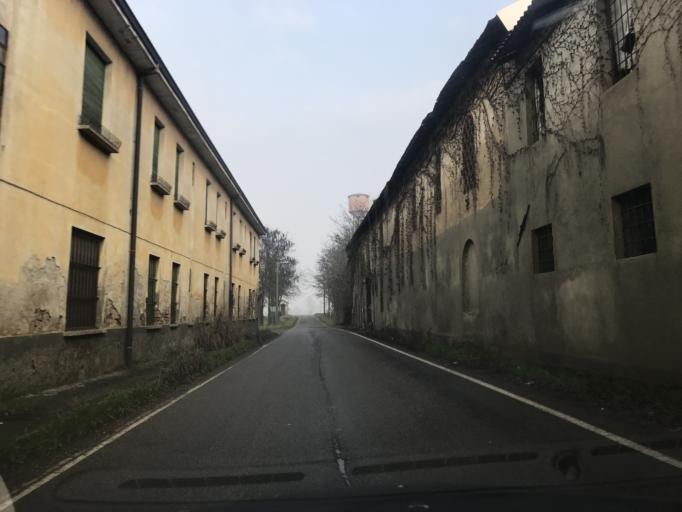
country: IT
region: Lombardy
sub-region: Provincia di Lodi
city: Bargano
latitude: 45.2437
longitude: 9.4607
